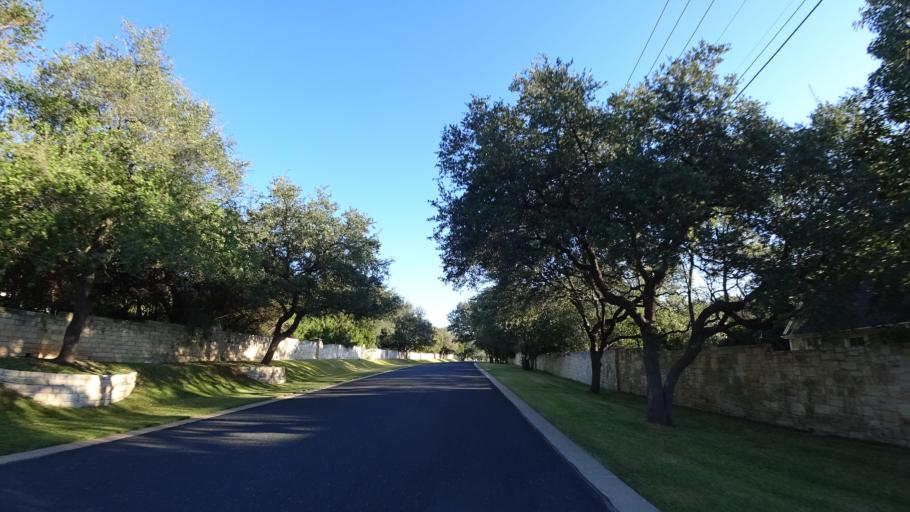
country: US
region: Texas
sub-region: Travis County
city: West Lake Hills
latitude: 30.3371
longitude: -97.8115
